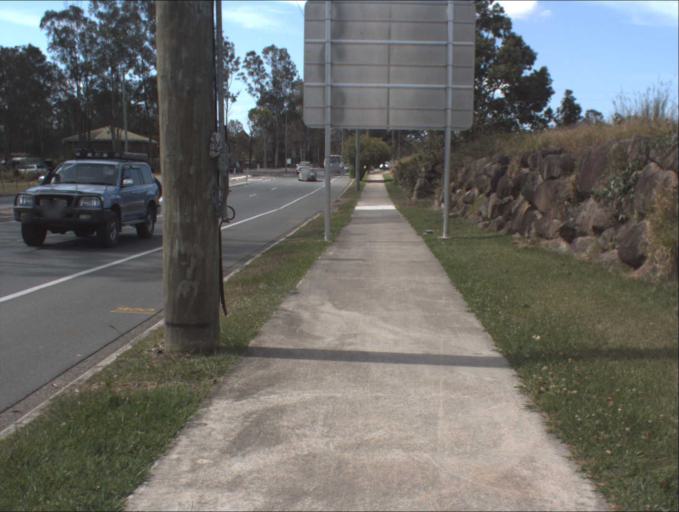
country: AU
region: Queensland
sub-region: Logan
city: Slacks Creek
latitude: -27.6615
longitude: 153.1408
